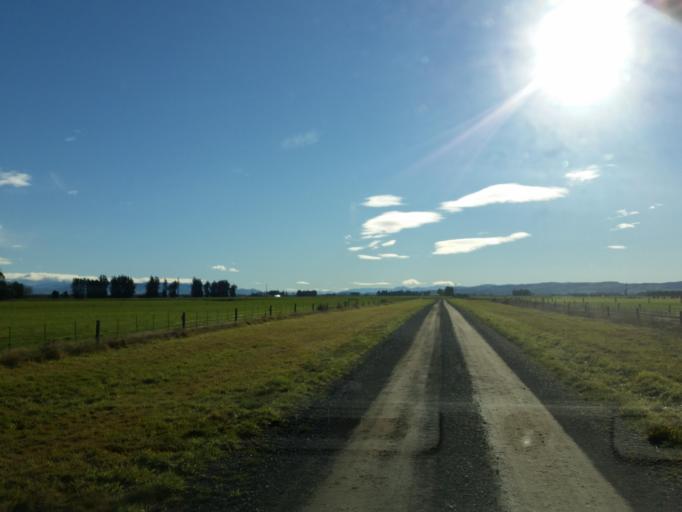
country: NZ
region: Southland
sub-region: Southland District
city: Winton
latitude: -46.1024
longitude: 168.1164
